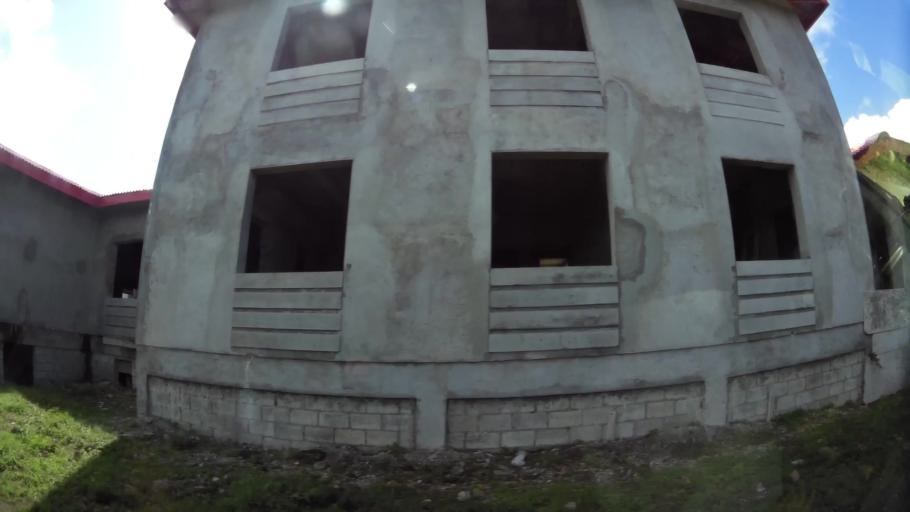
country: DM
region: Saint John
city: Portsmouth
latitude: 15.5852
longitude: -61.4662
